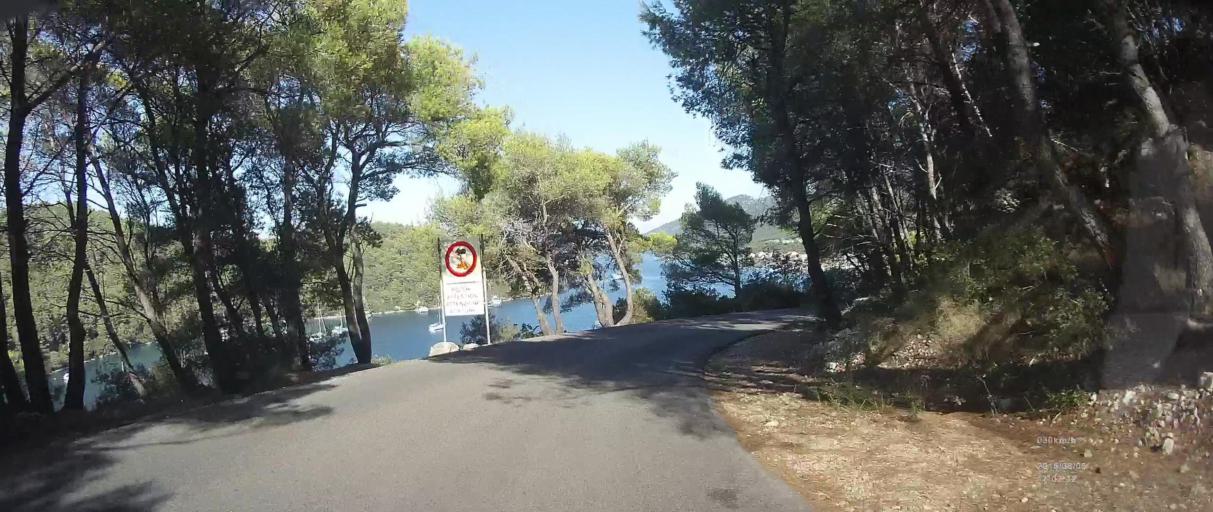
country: HR
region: Dubrovacko-Neretvanska
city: Blato
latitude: 42.7897
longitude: 17.3727
